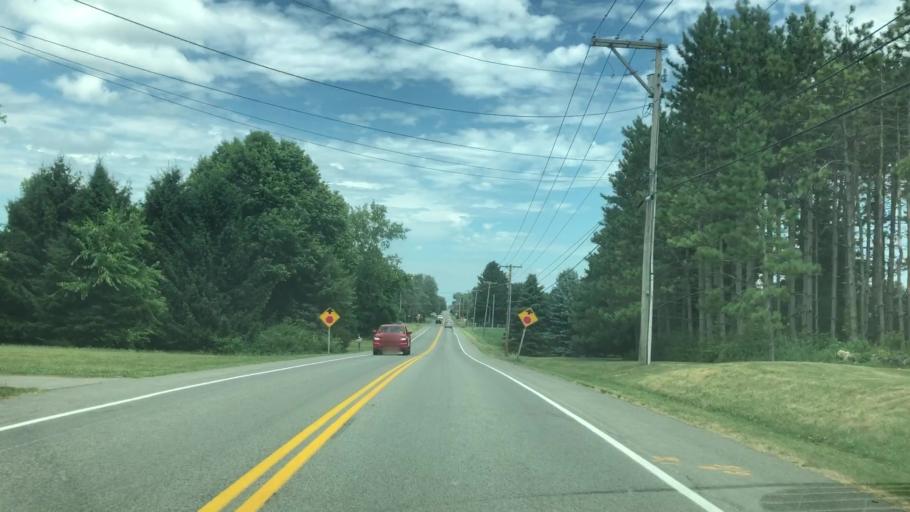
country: US
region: New York
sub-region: Monroe County
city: Webster
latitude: 43.1573
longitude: -77.4005
